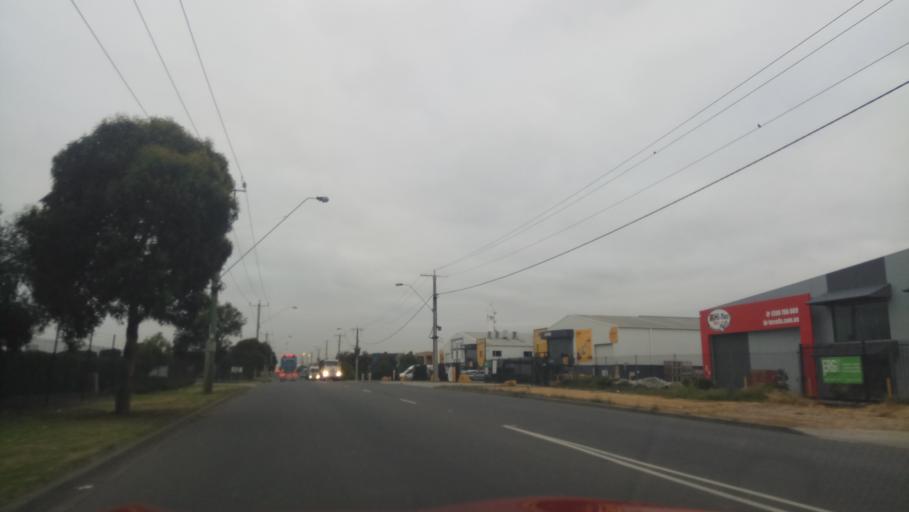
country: AU
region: Victoria
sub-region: Hobsons Bay
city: Laverton
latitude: -37.8496
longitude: 144.7898
